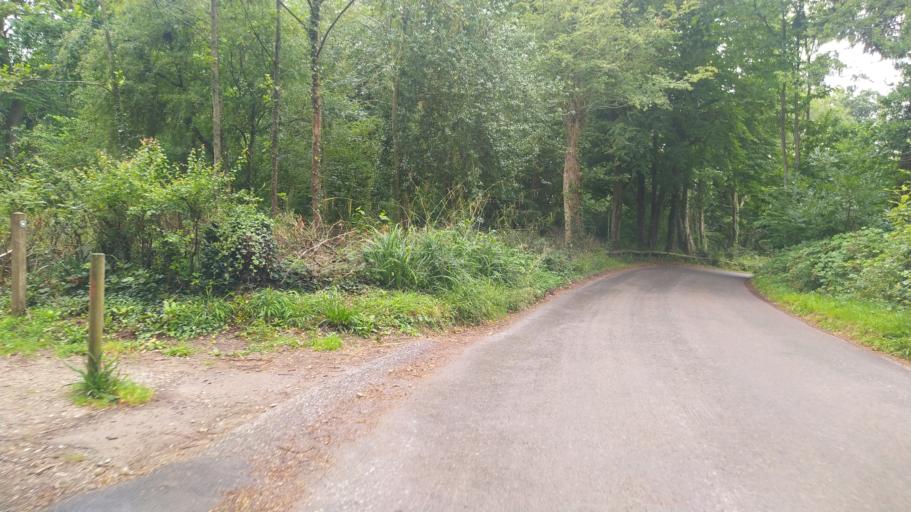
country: GB
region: England
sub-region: Hampshire
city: Hedge End
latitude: 50.8963
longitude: -1.2939
